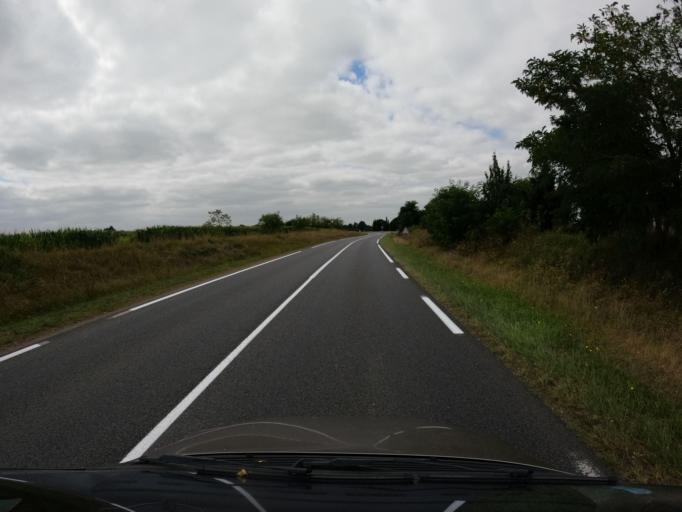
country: FR
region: Poitou-Charentes
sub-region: Departement de la Vienne
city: Charroux
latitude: 46.1530
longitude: 0.3754
